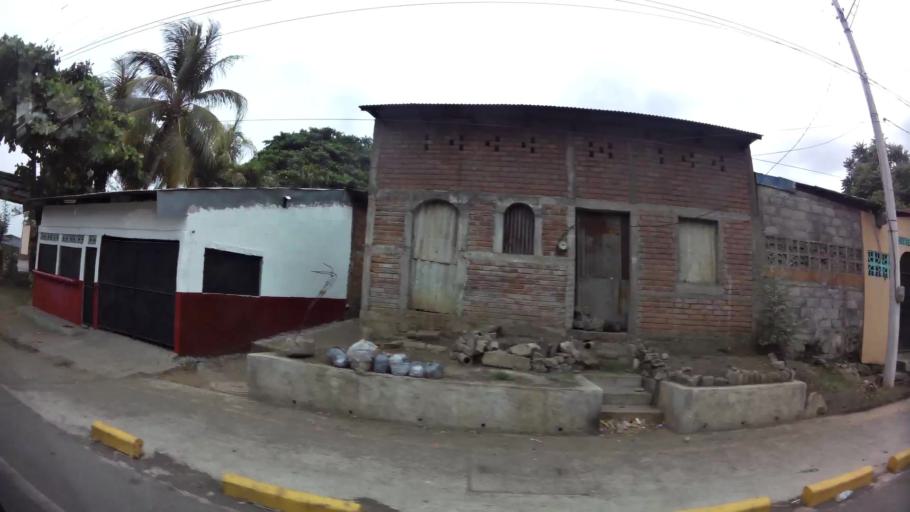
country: NI
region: Leon
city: Leon
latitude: 12.4543
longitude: -86.8648
